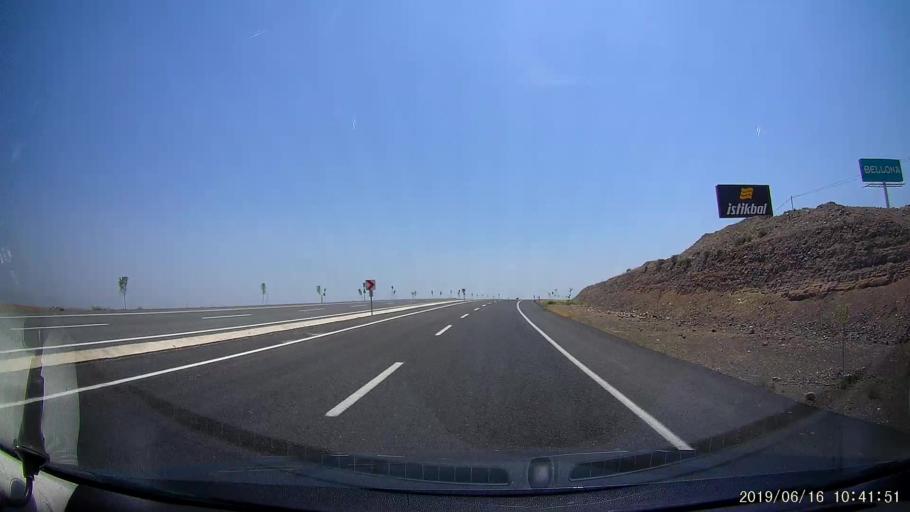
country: AM
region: Armavir
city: Shenavan
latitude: 40.0455
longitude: 43.7940
